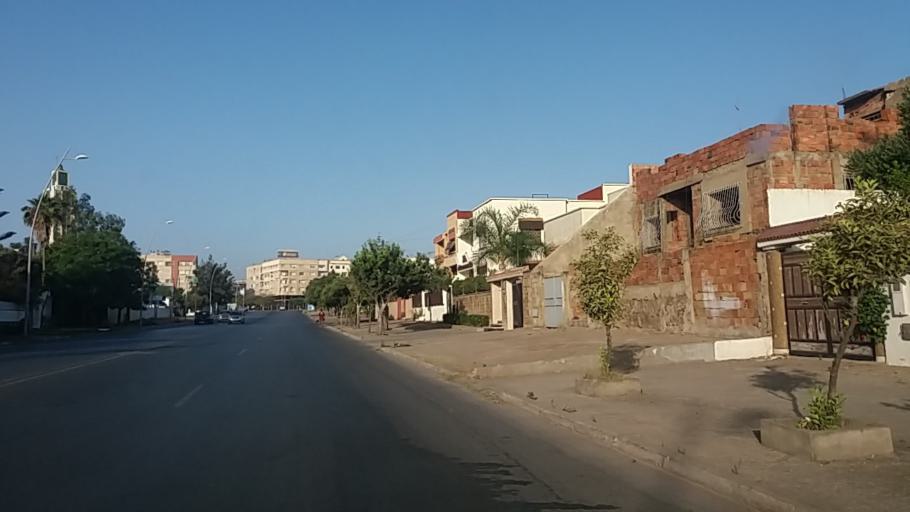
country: MA
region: Gharb-Chrarda-Beni Hssen
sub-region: Kenitra Province
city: Kenitra
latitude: 34.2567
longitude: -6.6017
